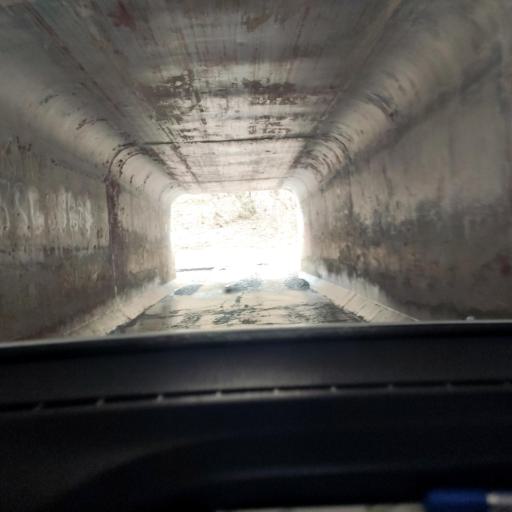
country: RU
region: Bashkortostan
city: Avdon
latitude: 54.6223
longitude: 55.5993
